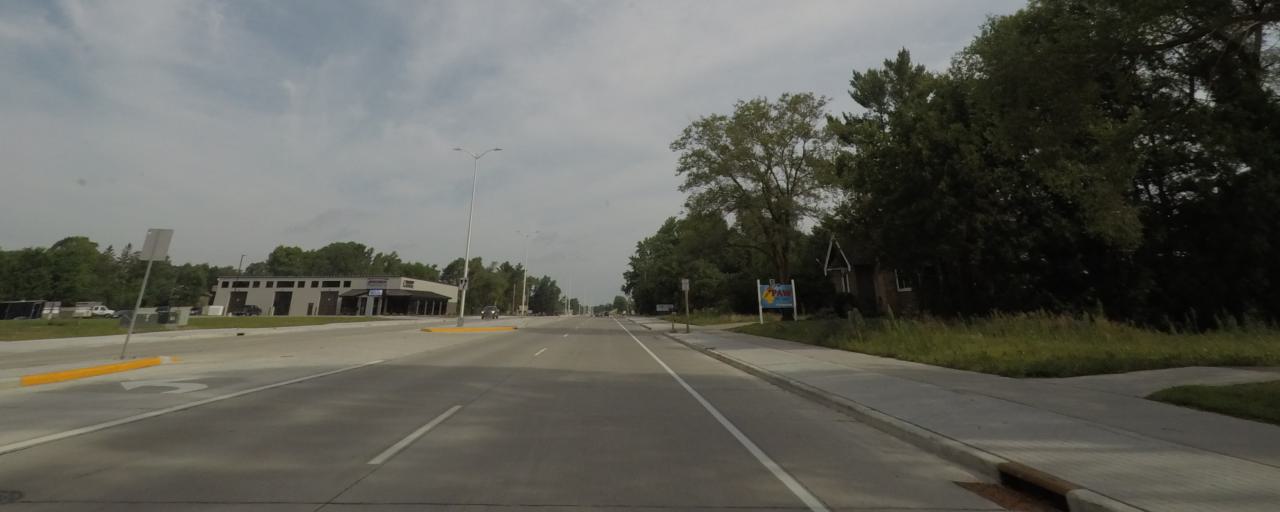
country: US
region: Wisconsin
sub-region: Portage County
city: Whiting
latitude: 44.4825
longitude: -89.5495
